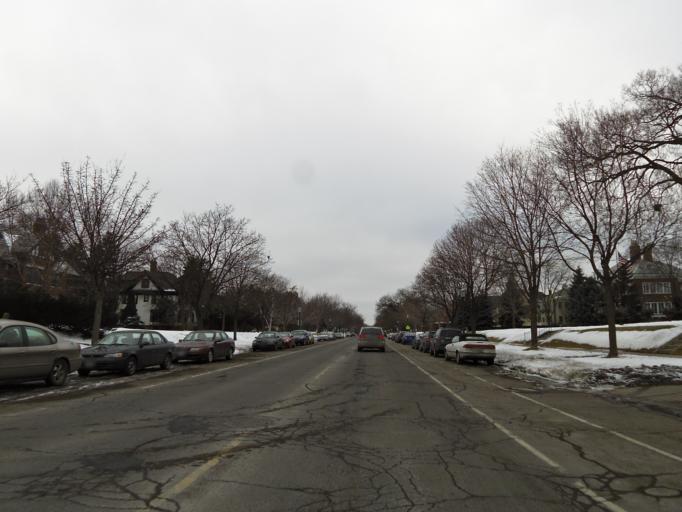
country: US
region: Minnesota
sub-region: Dakota County
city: West Saint Paul
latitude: 44.9414
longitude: -93.1397
